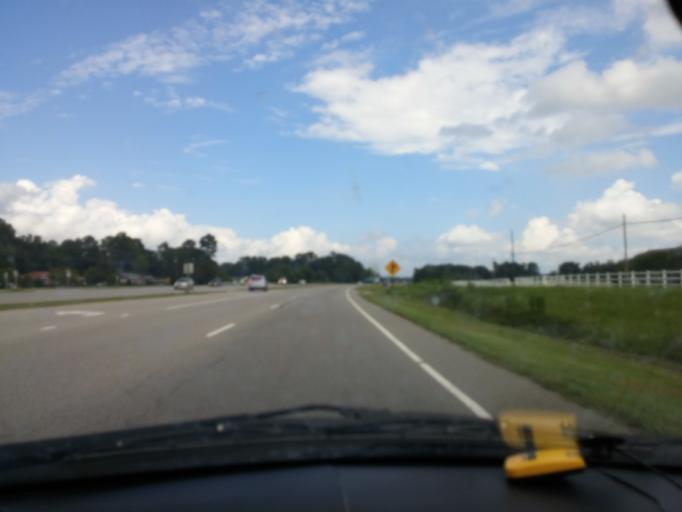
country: US
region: North Carolina
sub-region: Pitt County
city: Grifton
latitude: 35.3601
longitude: -77.4636
